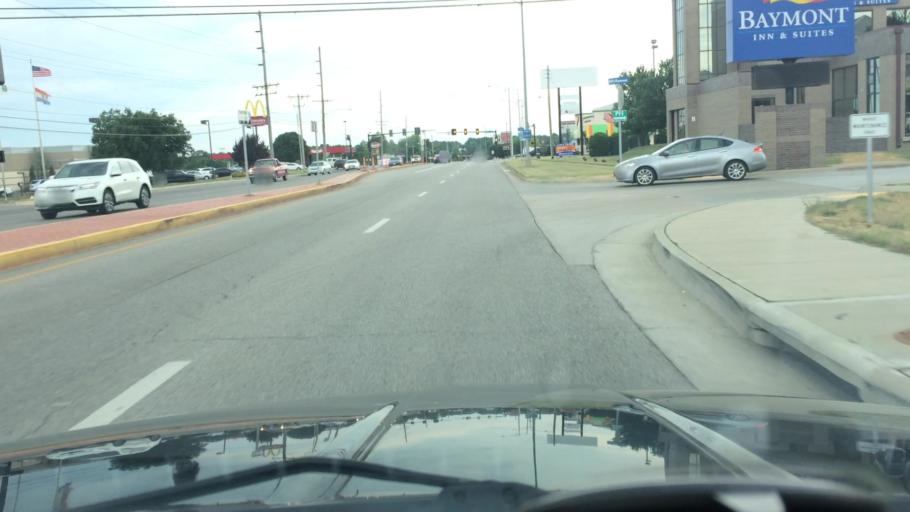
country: US
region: Missouri
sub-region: Greene County
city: Springfield
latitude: 37.1581
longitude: -93.2262
